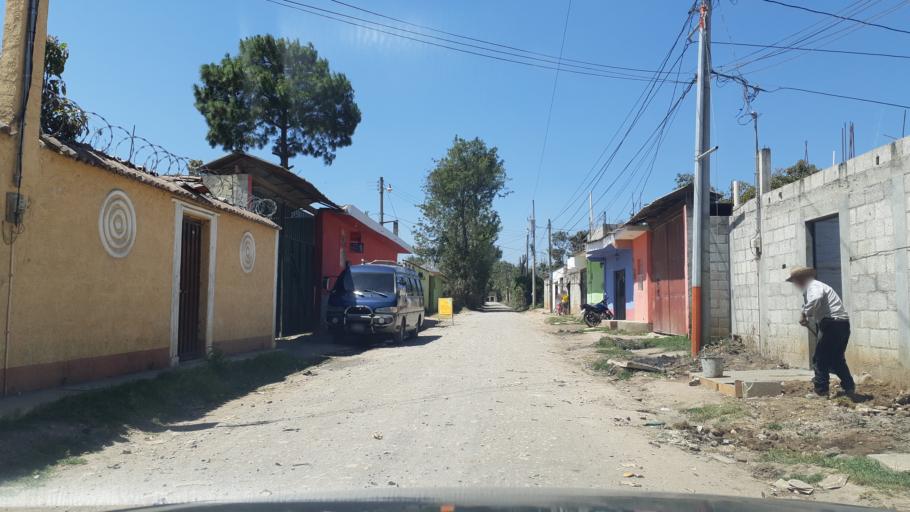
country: GT
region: Chimaltenango
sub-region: Municipio de Chimaltenango
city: Chimaltenango
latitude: 14.6515
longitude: -90.8083
